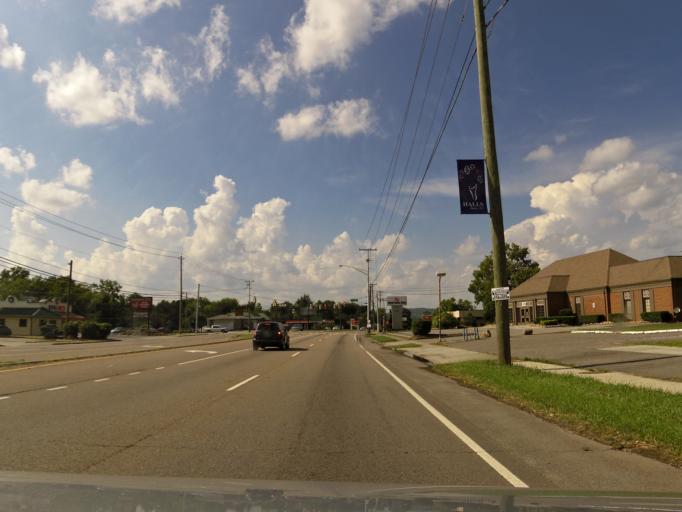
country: US
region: Tennessee
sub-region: Knox County
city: Knoxville
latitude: 36.0739
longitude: -83.9278
